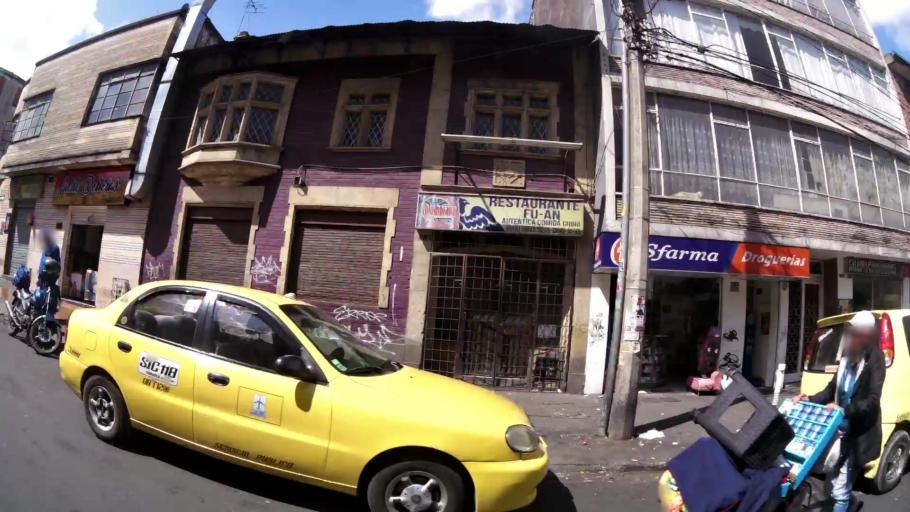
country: CO
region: Bogota D.C.
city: Bogota
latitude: 4.6122
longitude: -74.0755
